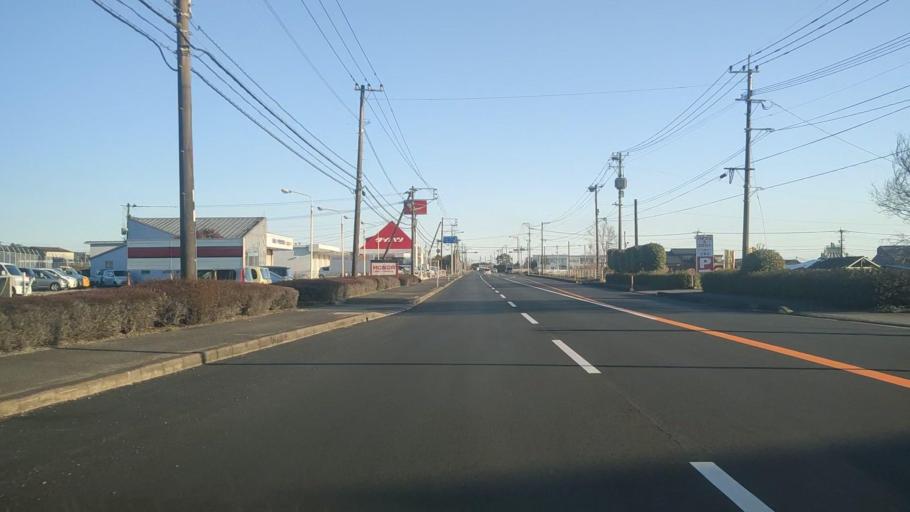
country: JP
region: Miyazaki
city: Takanabe
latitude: 32.2266
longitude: 131.5453
